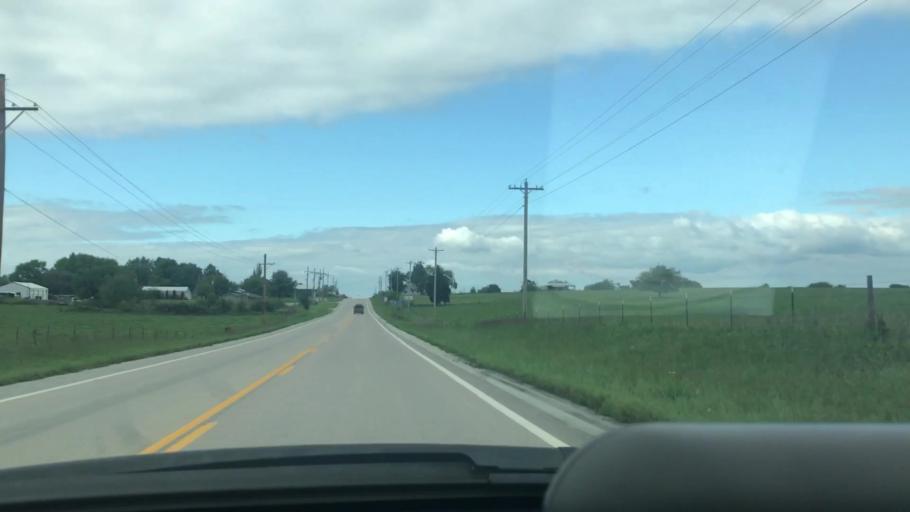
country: US
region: Missouri
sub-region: Hickory County
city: Hermitage
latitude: 37.9352
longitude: -93.2084
